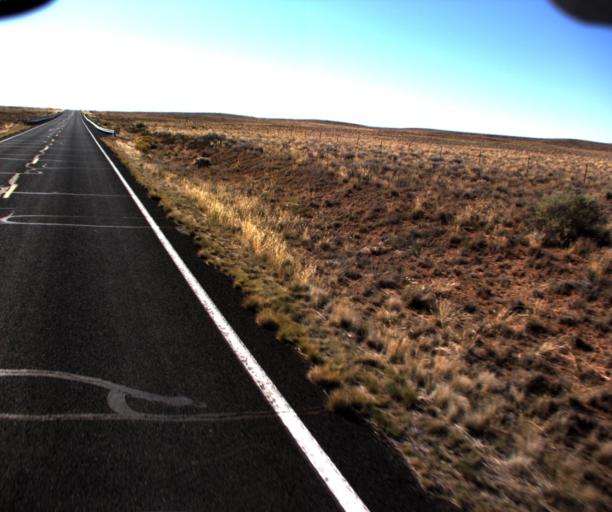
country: US
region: Arizona
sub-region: Navajo County
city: First Mesa
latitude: 35.6471
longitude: -110.4881
